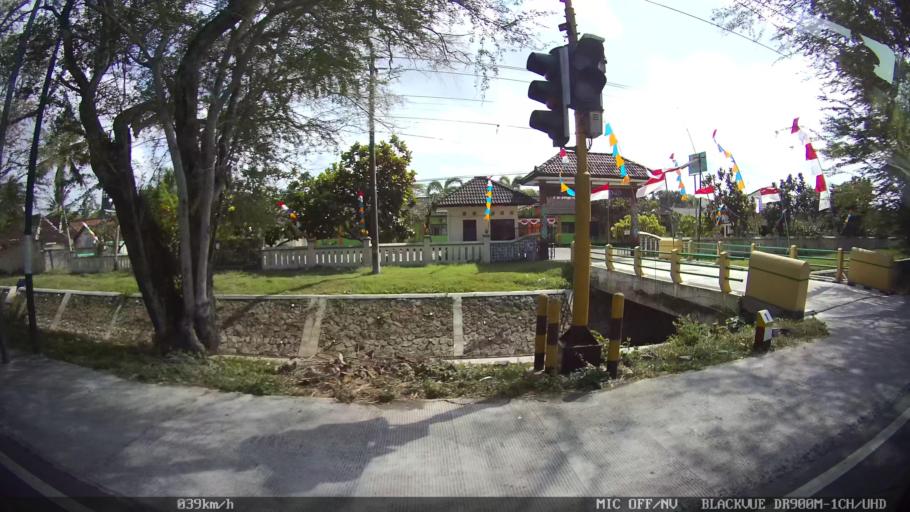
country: ID
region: Daerah Istimewa Yogyakarta
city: Srandakan
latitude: -7.8968
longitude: 110.1595
